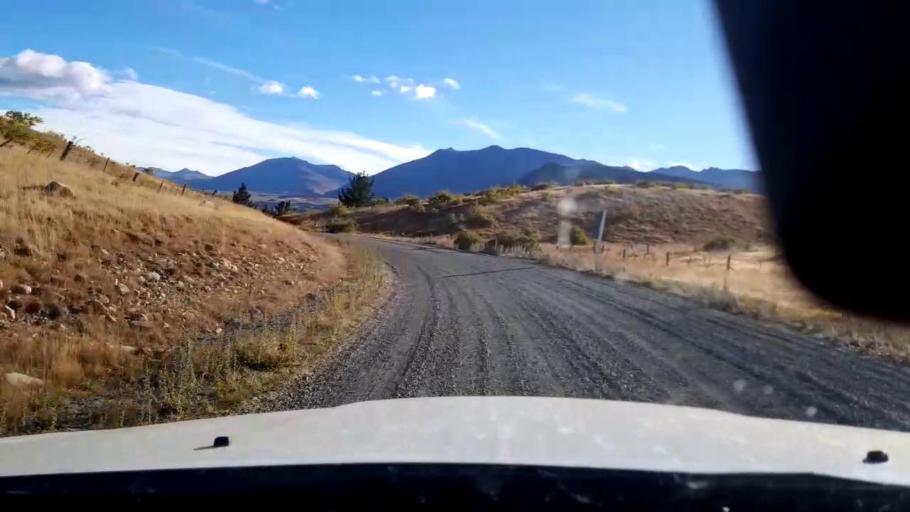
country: NZ
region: Canterbury
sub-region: Timaru District
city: Pleasant Point
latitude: -43.9654
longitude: 170.5217
